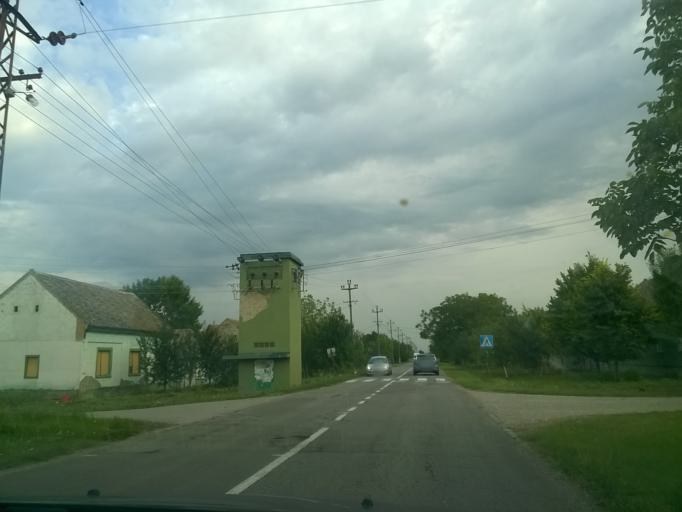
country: RS
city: Uzdin
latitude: 45.2090
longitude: 20.6281
